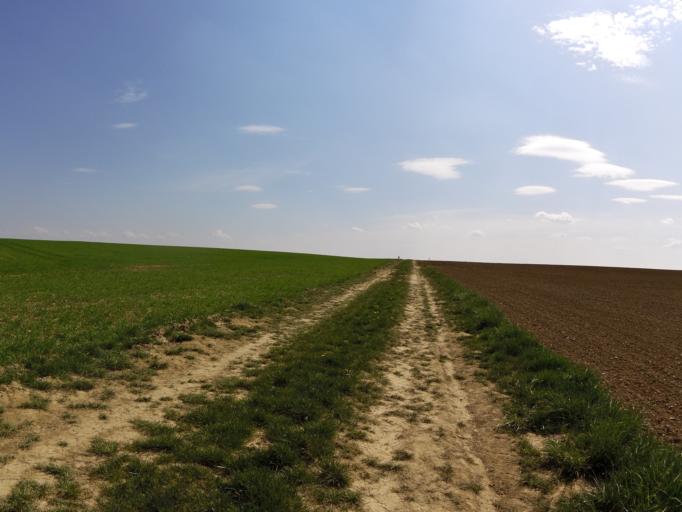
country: DE
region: Bavaria
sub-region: Regierungsbezirk Unterfranken
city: Giebelstadt
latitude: 49.6857
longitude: 9.9548
